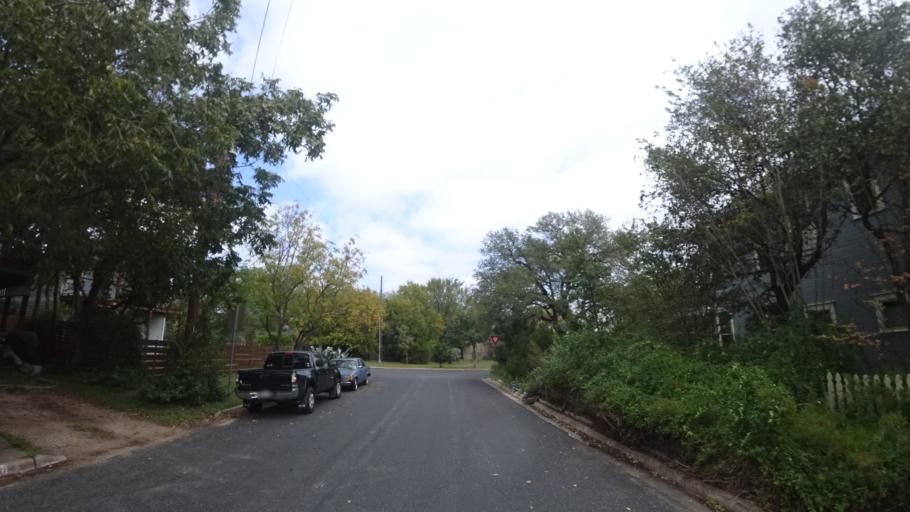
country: US
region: Texas
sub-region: Travis County
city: Austin
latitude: 30.2509
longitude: -97.7579
